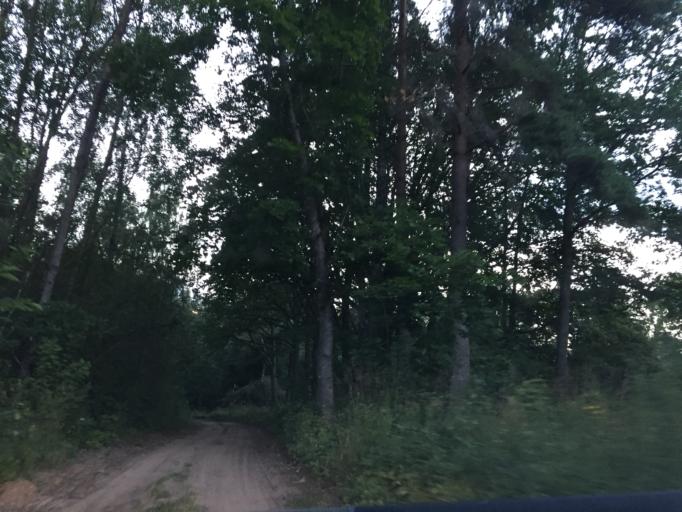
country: LV
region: Koknese
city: Koknese
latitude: 56.6190
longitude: 25.4976
